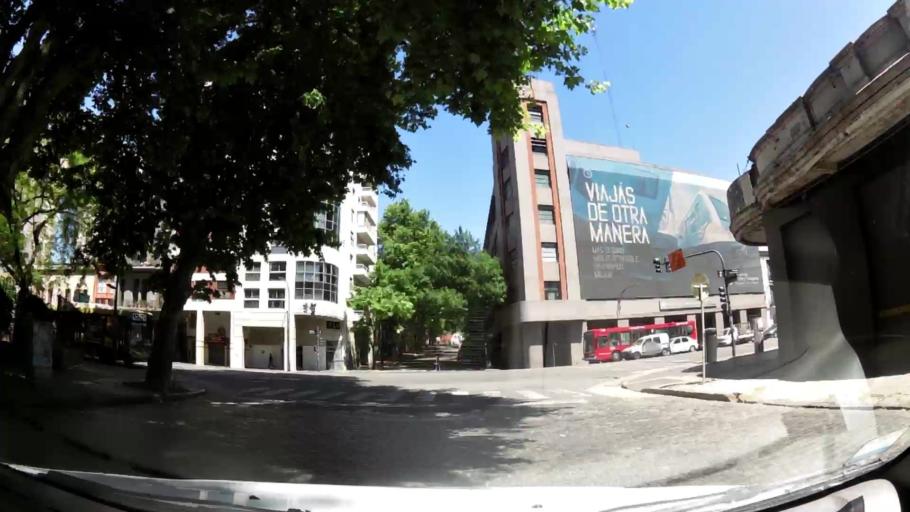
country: AR
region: Buenos Aires F.D.
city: Buenos Aires
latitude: -34.6205
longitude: -58.3679
